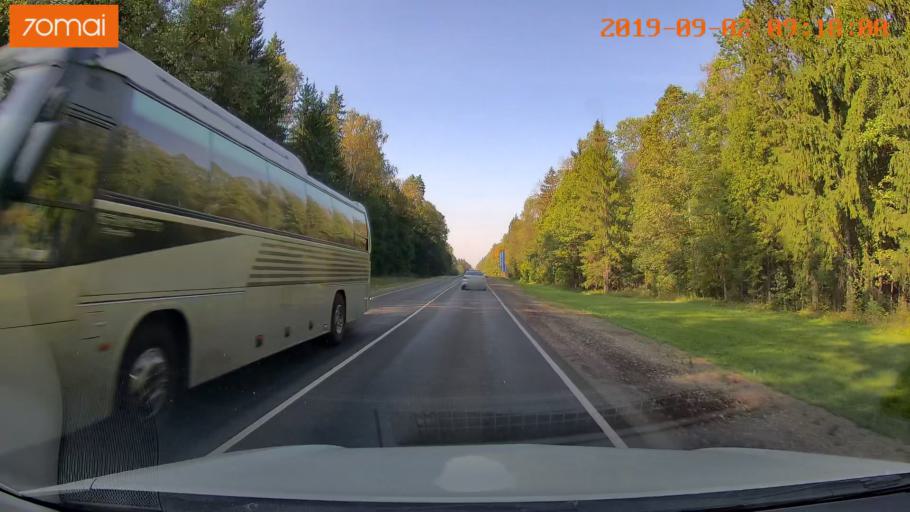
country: RU
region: Kaluga
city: Nikola-Lenivets
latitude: 54.8196
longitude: 35.4382
